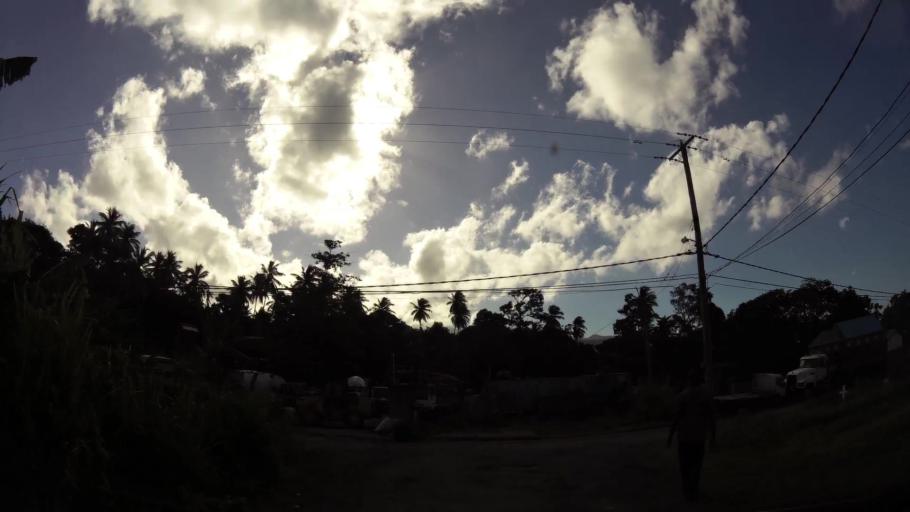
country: DM
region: Saint John
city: Portsmouth
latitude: 15.5795
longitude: -61.4561
